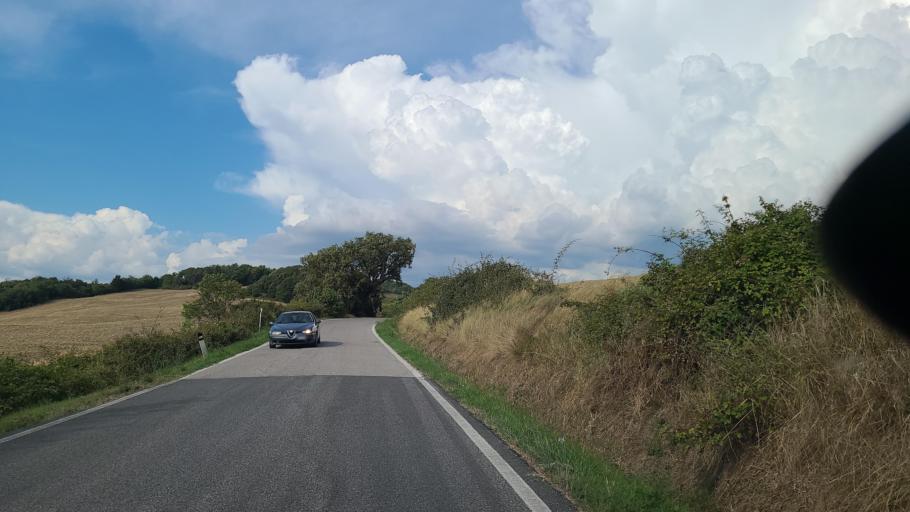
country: IT
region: Tuscany
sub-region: Provincia di Siena
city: San Gimignano
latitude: 43.4075
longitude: 10.9759
